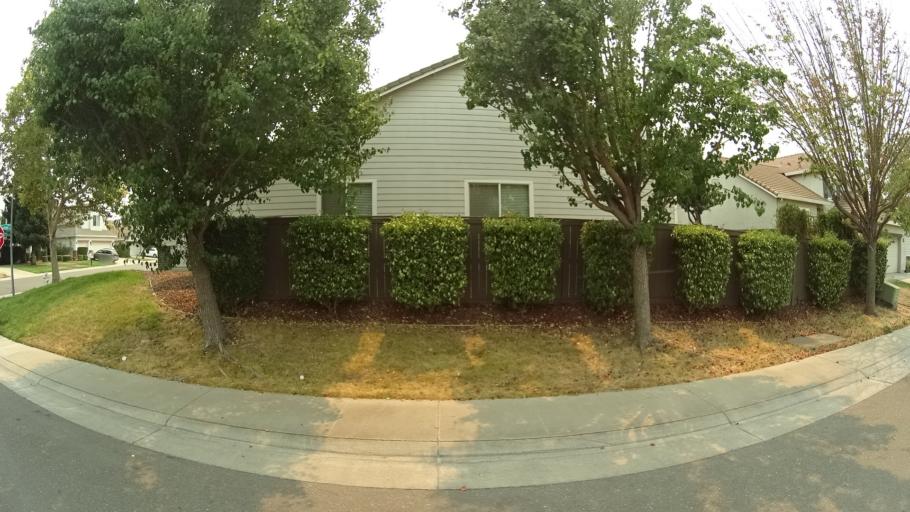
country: US
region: California
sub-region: Sacramento County
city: Laguna
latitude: 38.4066
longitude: -121.4260
